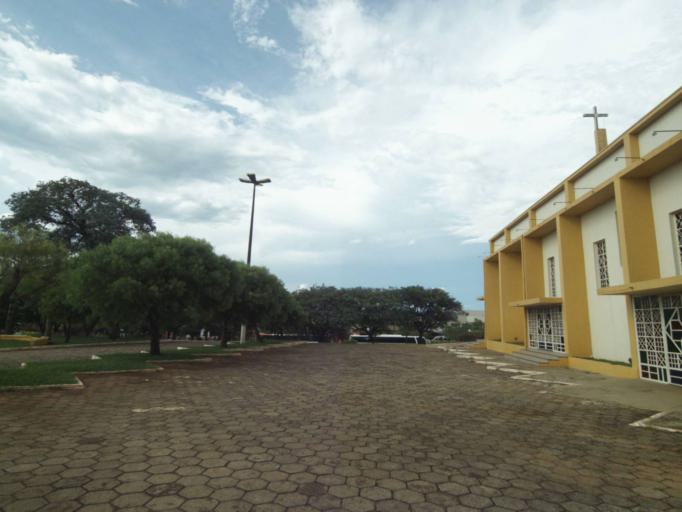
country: BR
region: Parana
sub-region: Guaraniacu
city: Guaraniacu
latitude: -25.1020
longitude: -52.8682
